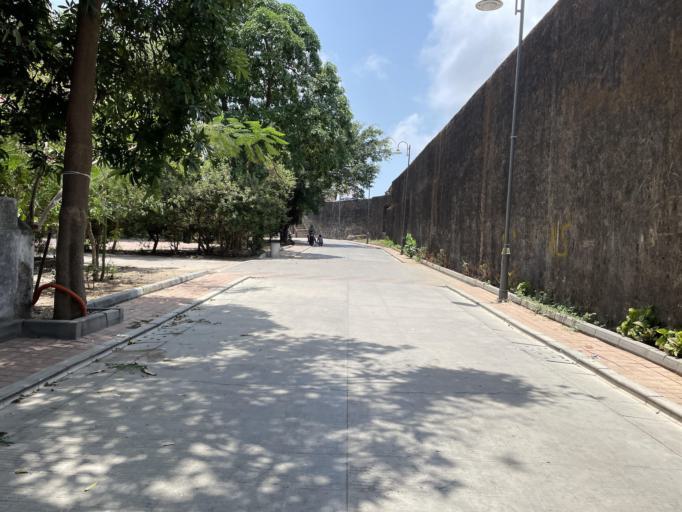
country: IN
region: Daman and Diu
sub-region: Daman District
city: Daman
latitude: 20.4099
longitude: 72.8321
